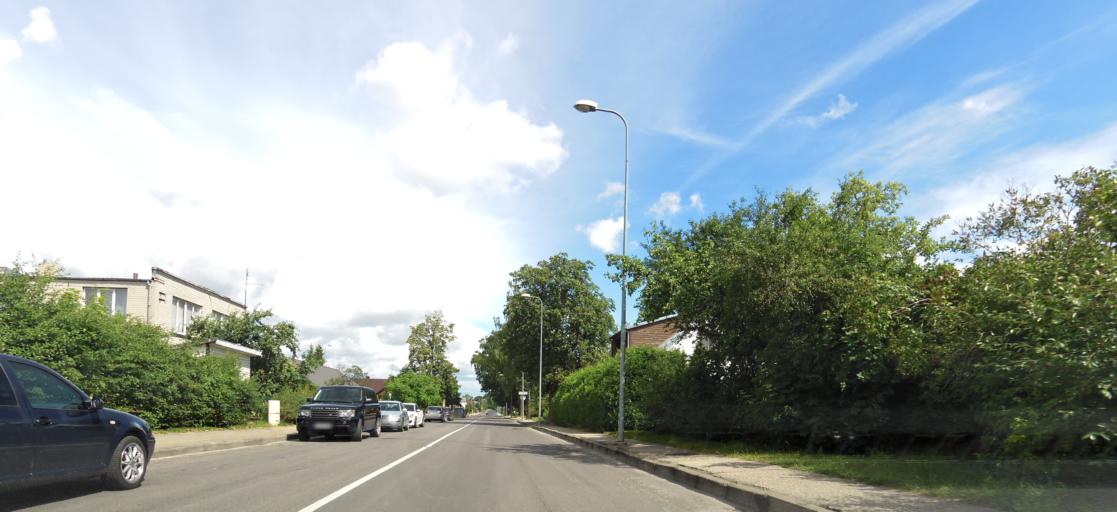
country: LT
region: Panevezys
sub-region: Birzai
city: Birzai
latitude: 56.1988
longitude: 24.7413
